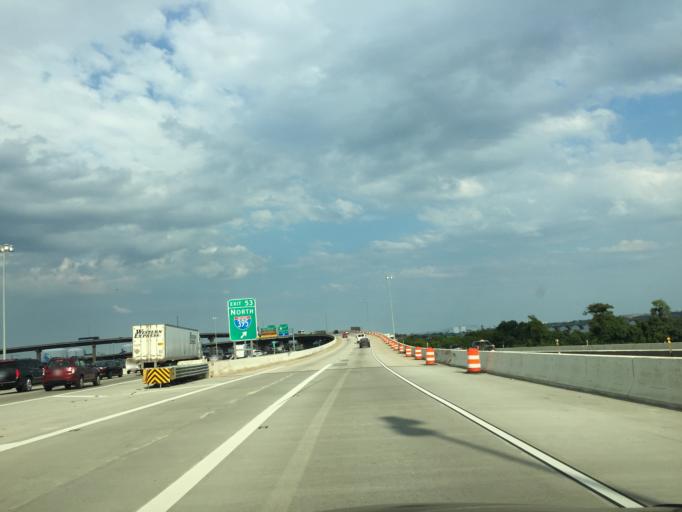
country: US
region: Maryland
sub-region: City of Baltimore
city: Baltimore
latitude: 39.2685
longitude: -76.6299
